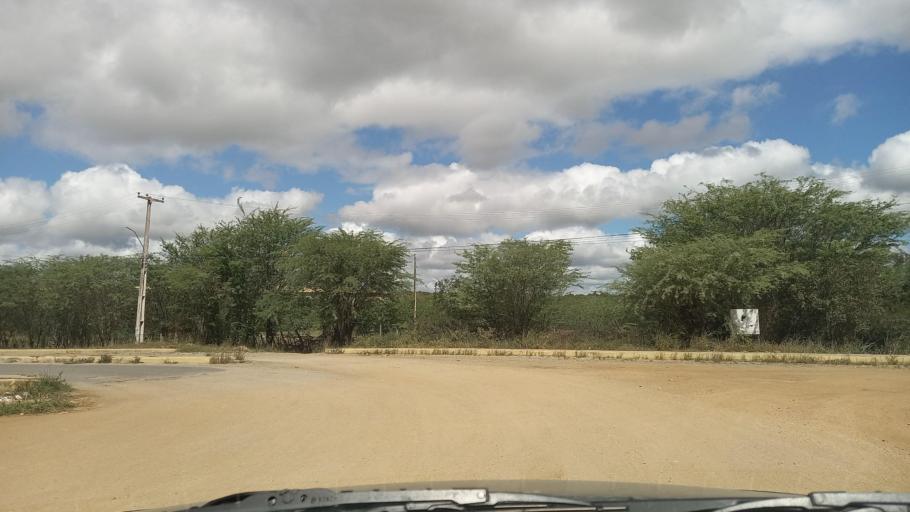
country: BR
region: Pernambuco
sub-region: Caruaru
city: Caruaru
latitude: -8.2422
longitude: -35.9844
